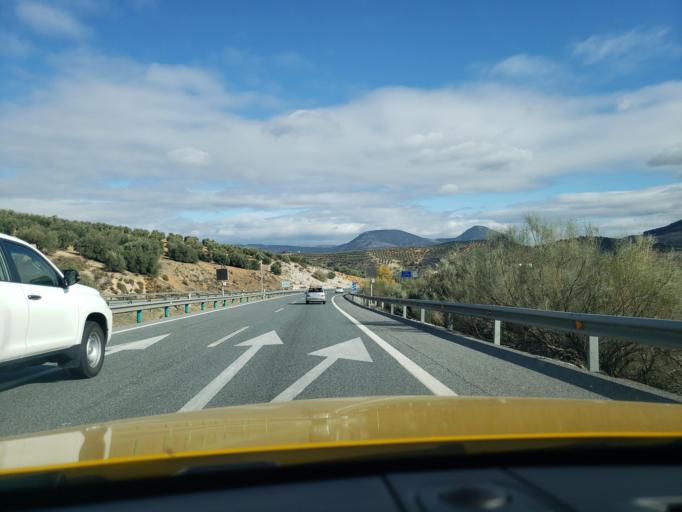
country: ES
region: Andalusia
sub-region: Provincia de Granada
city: Loja
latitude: 37.1578
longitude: -4.2178
